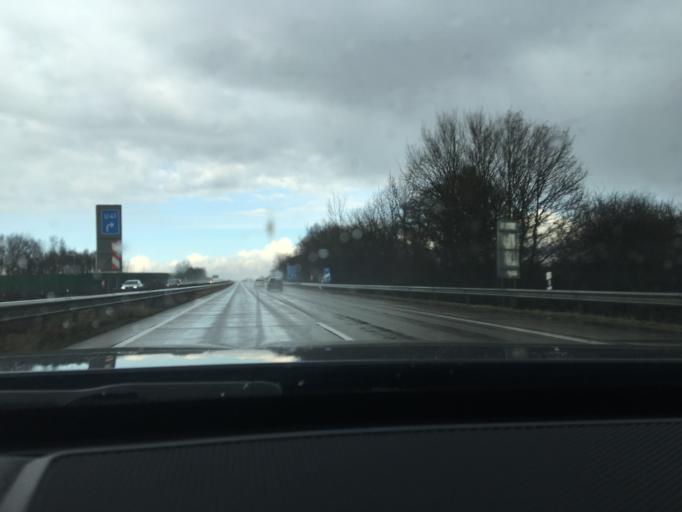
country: DE
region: Lower Saxony
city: Loxstedt
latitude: 53.4933
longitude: 8.6255
